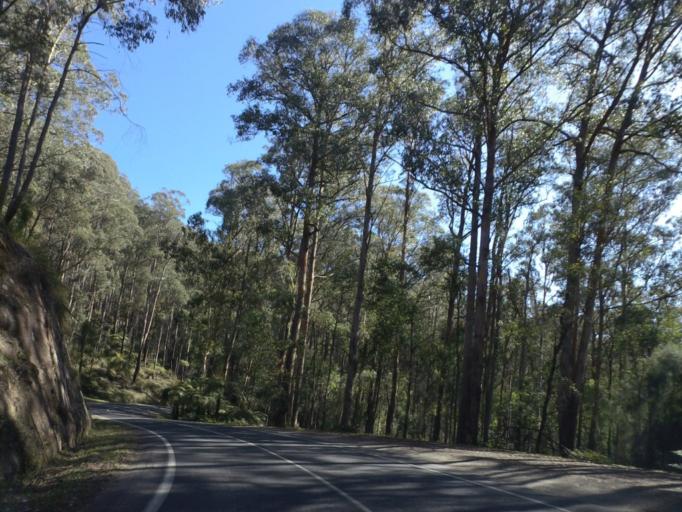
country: AU
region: Victoria
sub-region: Yarra Ranges
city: Millgrove
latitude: -37.8684
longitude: 145.7739
